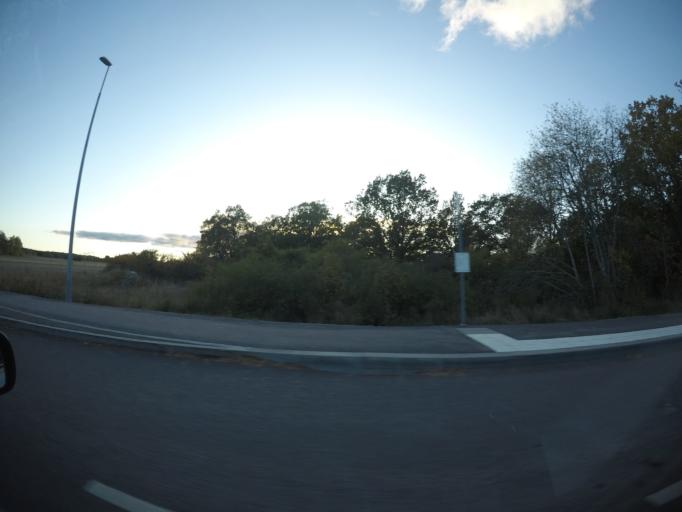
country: SE
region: Vaestmanland
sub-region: Vasteras
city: Vasteras
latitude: 59.5663
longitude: 16.5237
